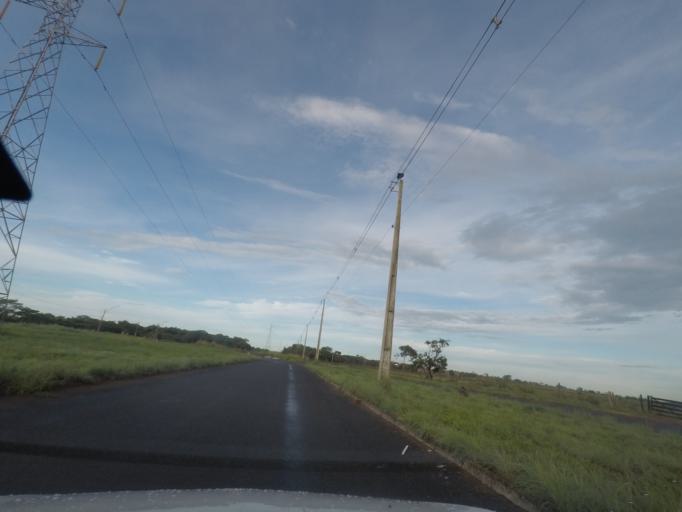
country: BR
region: Goias
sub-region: Trindade
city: Trindade
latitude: -16.7463
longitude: -49.3867
